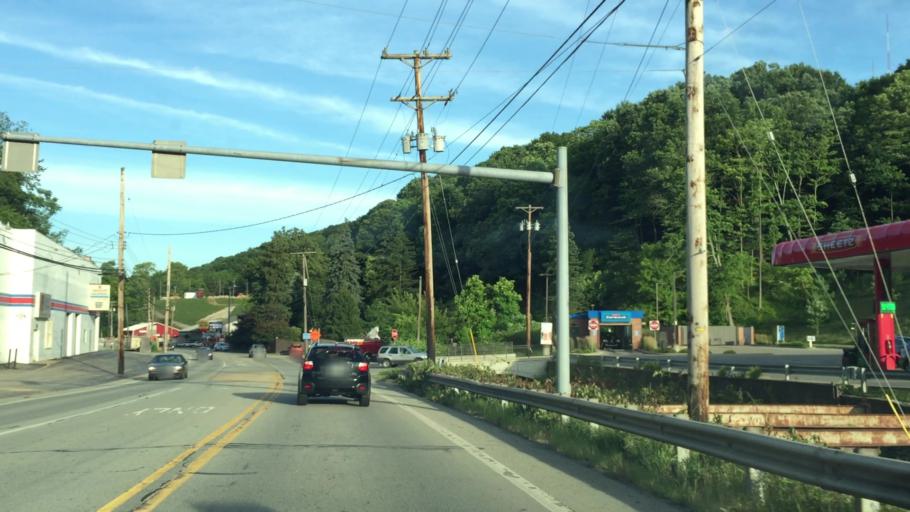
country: US
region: Pennsylvania
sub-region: Allegheny County
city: West View
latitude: 40.5154
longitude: -80.0093
